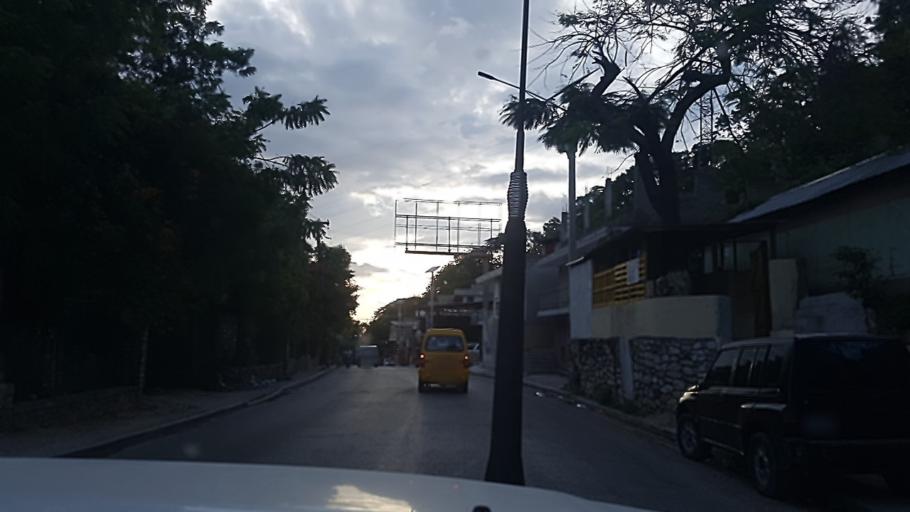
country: HT
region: Ouest
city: Petionville
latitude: 18.5248
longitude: -72.2954
